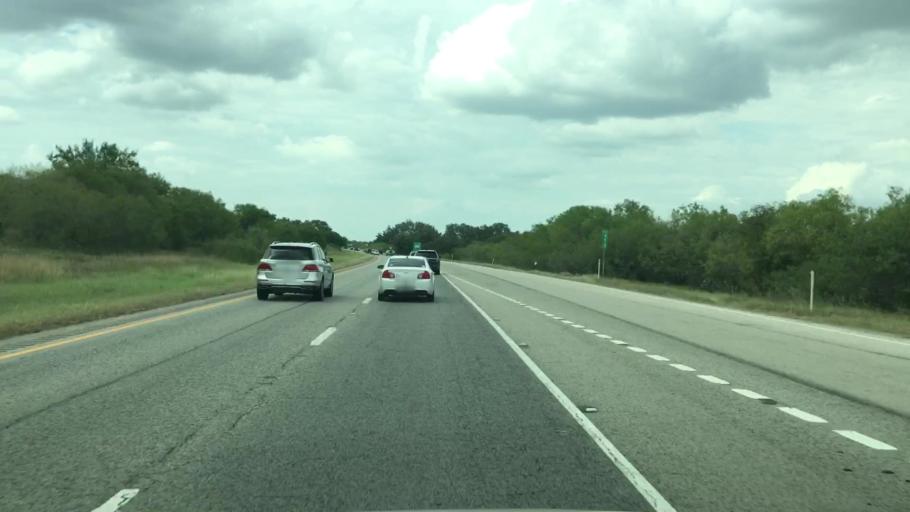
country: US
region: Texas
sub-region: Atascosa County
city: Pleasanton
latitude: 29.0393
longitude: -98.4315
